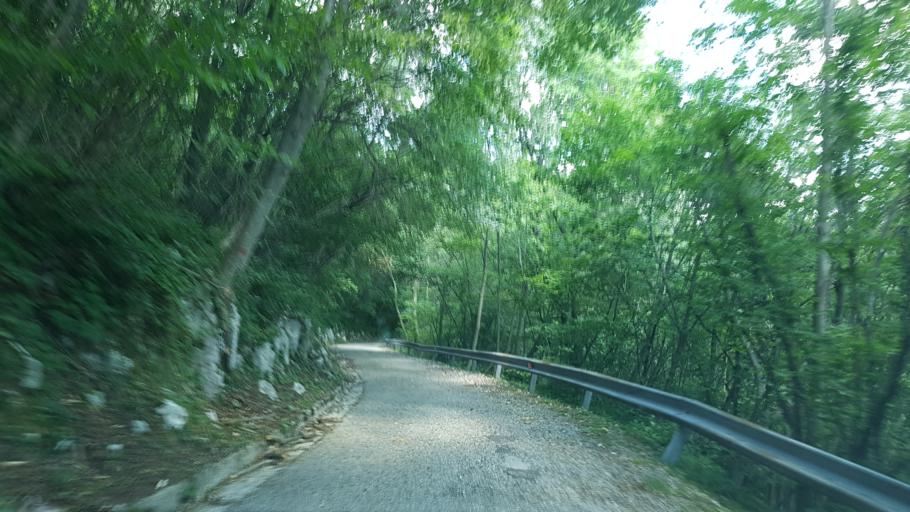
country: IT
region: Friuli Venezia Giulia
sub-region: Provincia di Udine
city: Nimis
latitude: 46.2383
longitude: 13.2659
